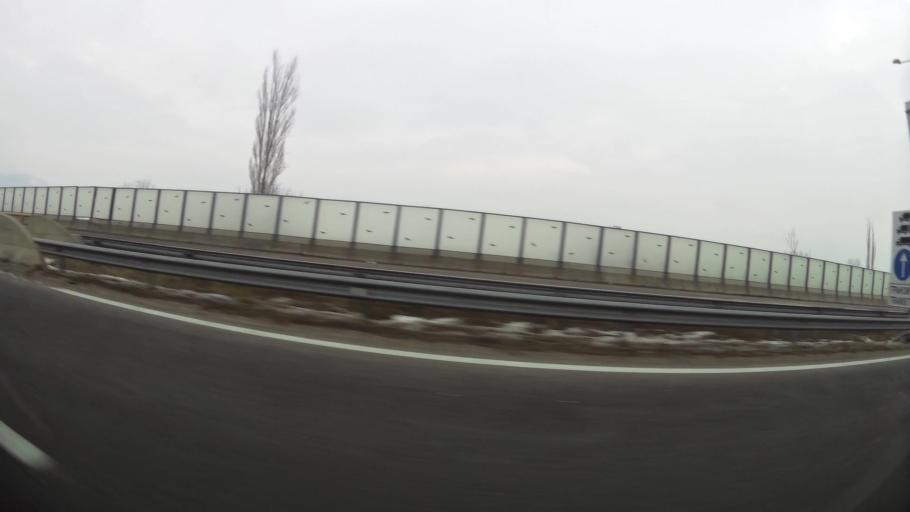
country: MK
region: Cucer-Sandevo
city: Chucher - Sandevo
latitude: 42.0544
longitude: 21.3596
